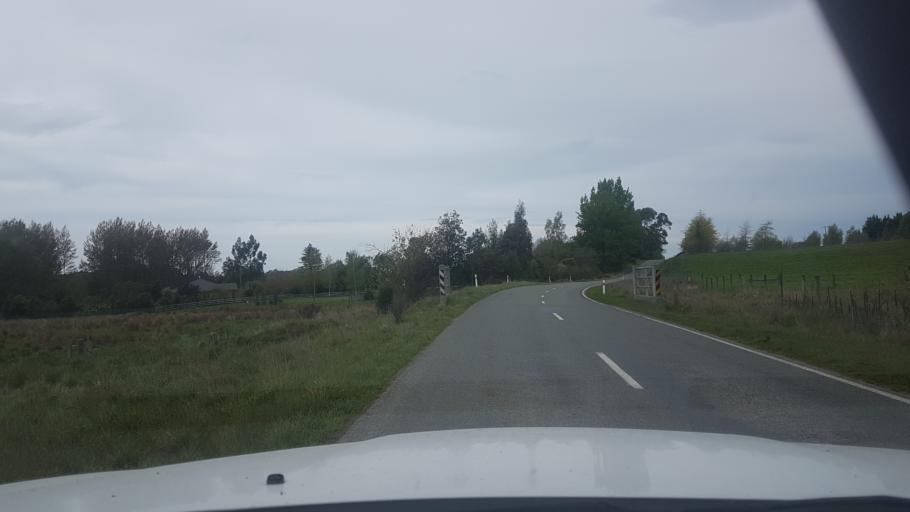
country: NZ
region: Canterbury
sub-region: Timaru District
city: Pleasant Point
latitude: -44.0798
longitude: 171.1780
